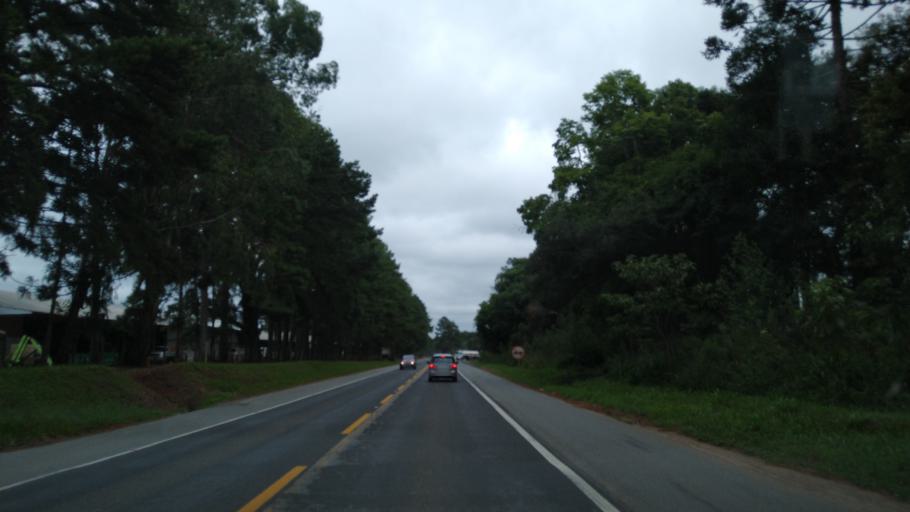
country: BR
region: Santa Catarina
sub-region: Tres Barras
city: Tres Barras
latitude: -26.1622
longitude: -50.1268
